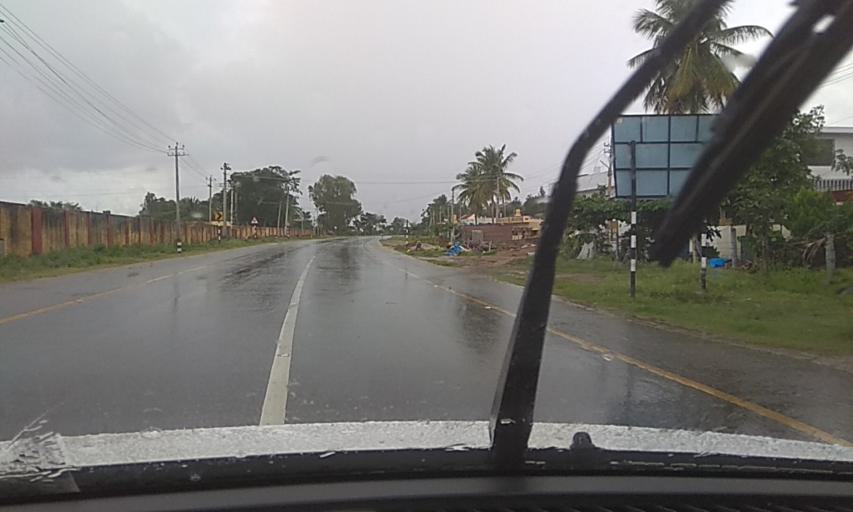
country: IN
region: Karnataka
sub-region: Ramanagara
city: Channapatna
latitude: 12.7682
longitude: 77.0611
